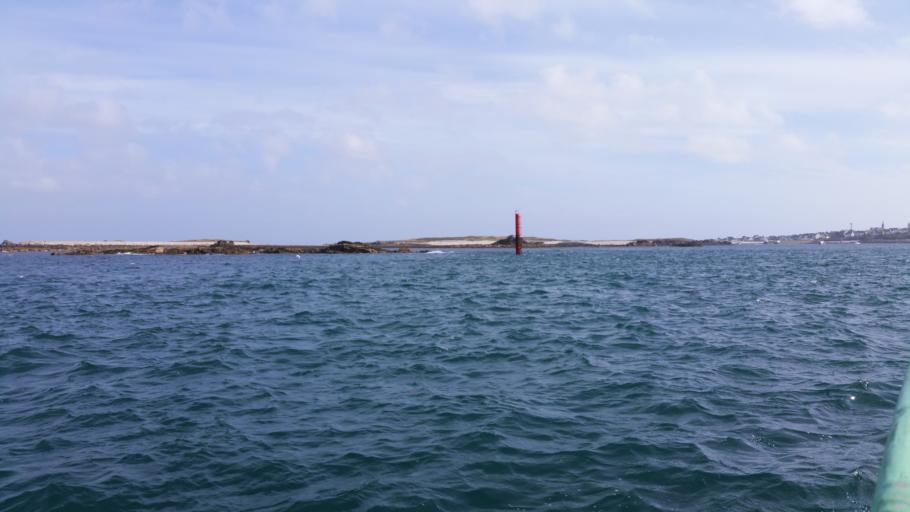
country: FR
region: Brittany
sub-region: Departement du Finistere
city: Le Conquet
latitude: 48.4106
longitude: -4.9507
